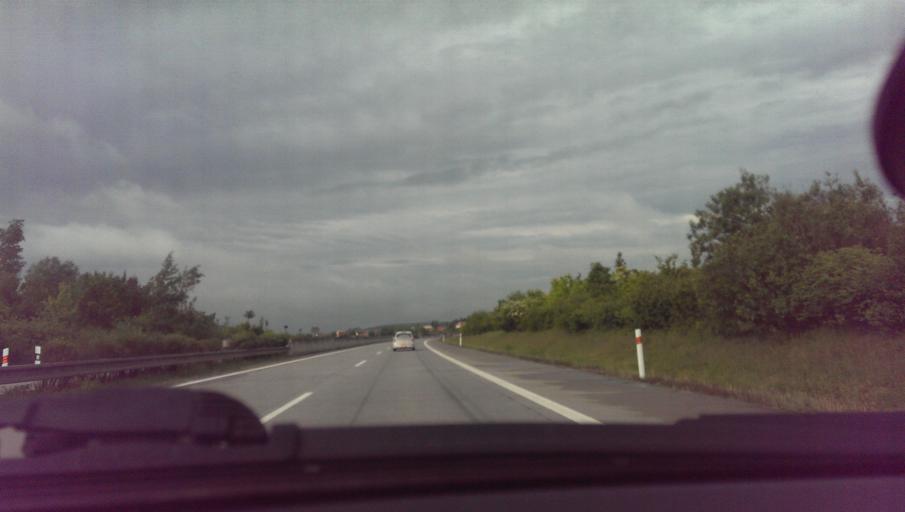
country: CZ
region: South Moravian
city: Ivanovice na Hane
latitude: 49.2833
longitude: 17.0792
